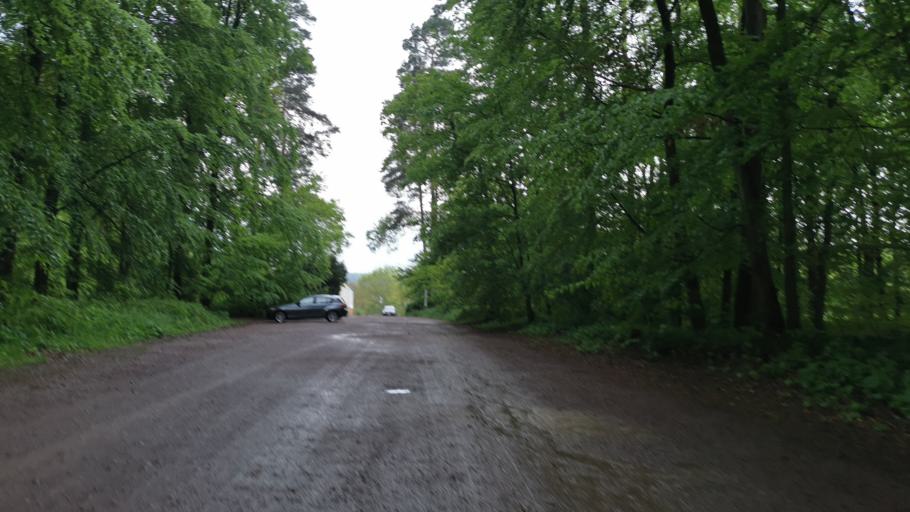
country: DE
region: Saarland
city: Sankt Ingbert
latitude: 49.2683
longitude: 7.1749
